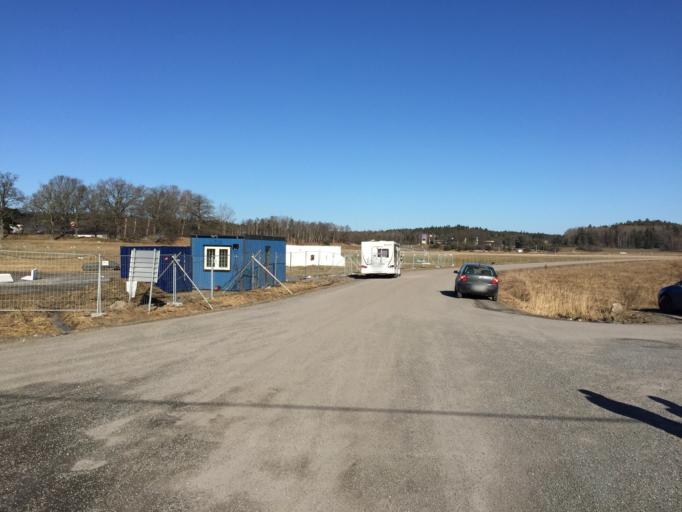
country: SE
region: Stockholm
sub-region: Sodertalje Kommun
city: Pershagen
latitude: 59.0822
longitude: 17.5989
